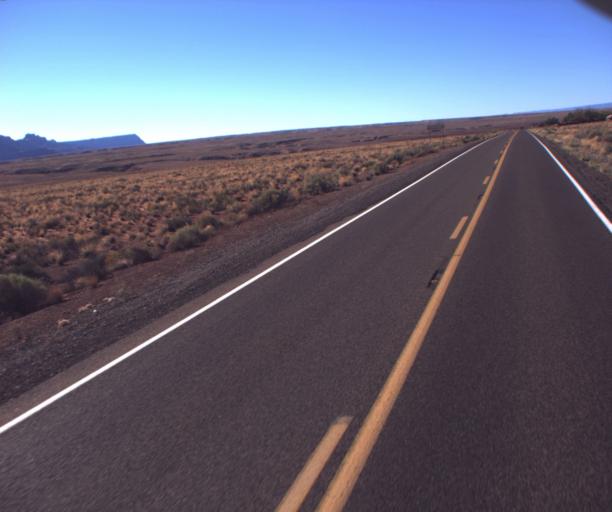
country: US
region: Arizona
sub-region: Coconino County
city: Page
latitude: 36.7938
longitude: -111.6815
